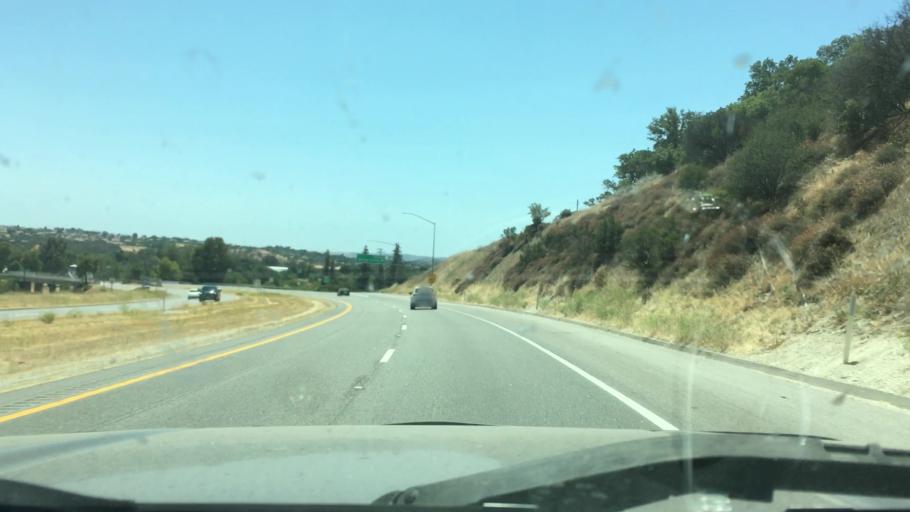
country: US
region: California
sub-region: San Luis Obispo County
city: Paso Robles
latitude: 35.6562
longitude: -120.6977
